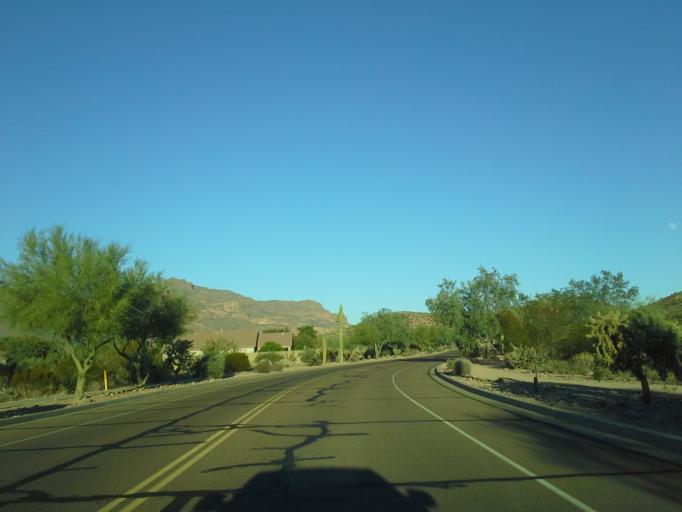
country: US
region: Arizona
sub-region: Pinal County
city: Apache Junction
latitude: 33.3757
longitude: -111.4665
